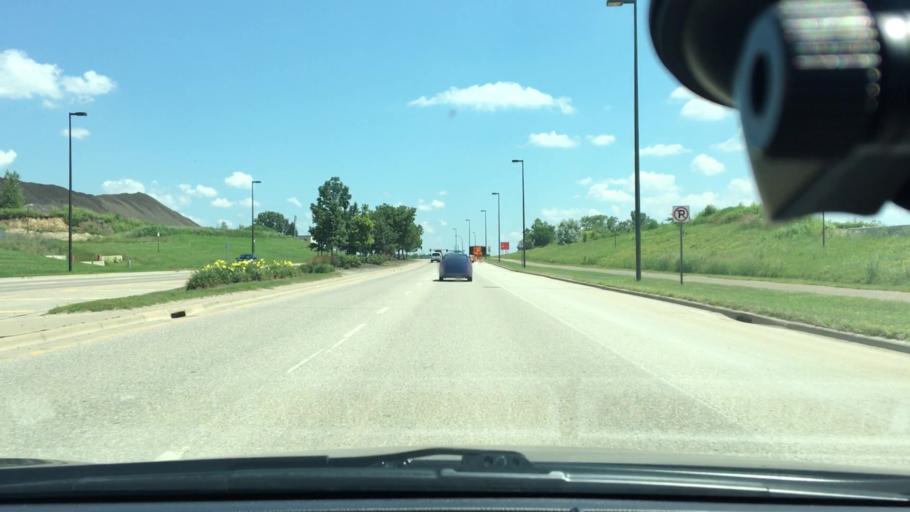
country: US
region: Minnesota
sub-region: Hennepin County
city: Osseo
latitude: 45.0945
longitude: -93.4105
